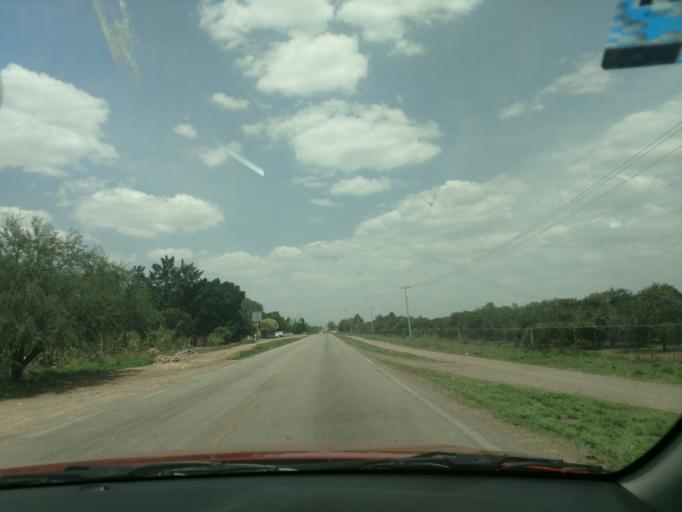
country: MX
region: San Luis Potosi
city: Ciudad Fernandez
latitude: 21.9498
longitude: -100.0618
